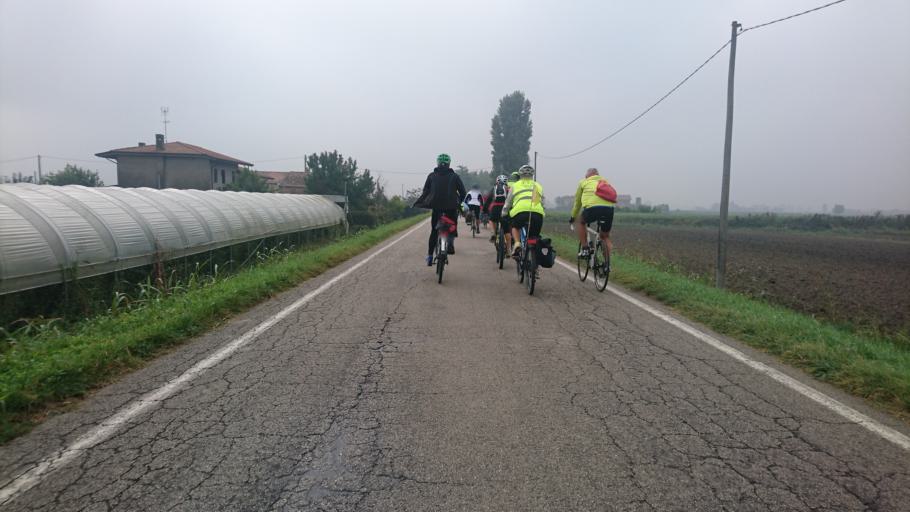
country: IT
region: Veneto
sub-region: Provincia di Padova
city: Pozzonovo
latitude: 45.1646
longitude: 11.7881
